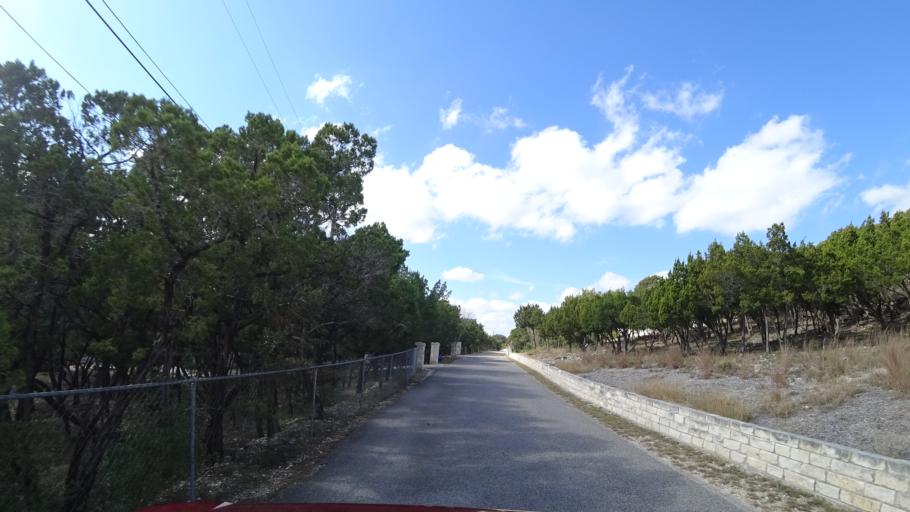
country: US
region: Texas
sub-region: Williamson County
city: Anderson Mill
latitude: 30.4195
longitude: -97.8030
